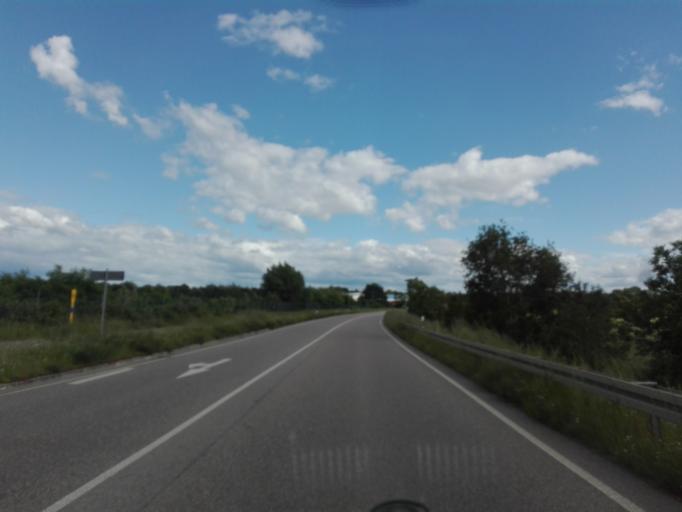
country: DE
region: Baden-Wuerttemberg
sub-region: Karlsruhe Region
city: Philippsburg
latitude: 49.2181
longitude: 8.4699
